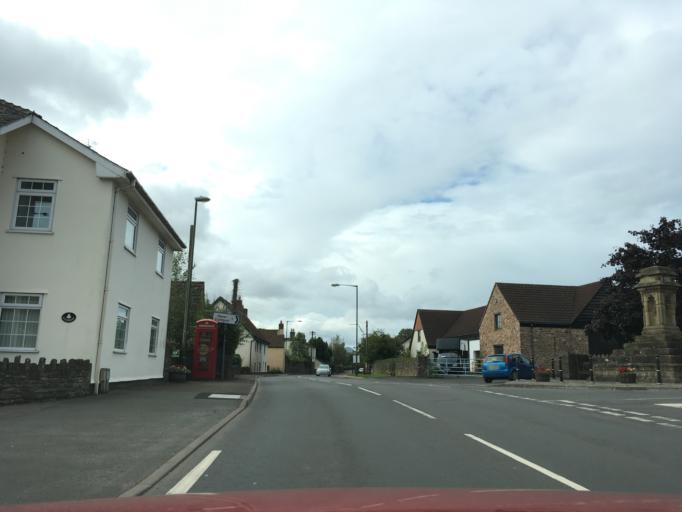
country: GB
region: England
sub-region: Gloucestershire
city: Lydney
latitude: 51.7138
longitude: -2.5549
